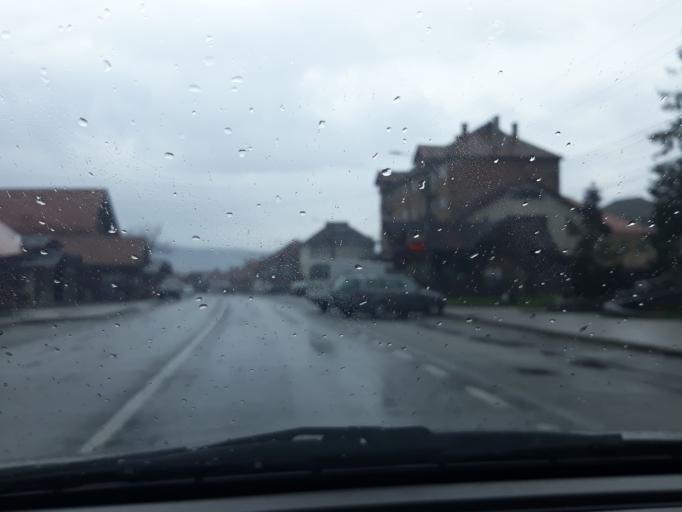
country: RO
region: Harghita
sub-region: Comuna Corund
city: Corund
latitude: 46.4719
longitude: 25.1848
